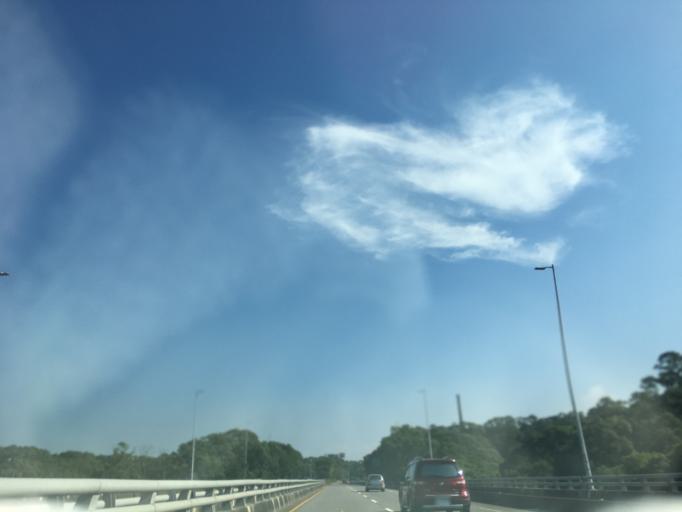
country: TW
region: Taiwan
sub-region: Hsinchu
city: Hsinchu
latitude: 24.7854
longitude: 120.9511
